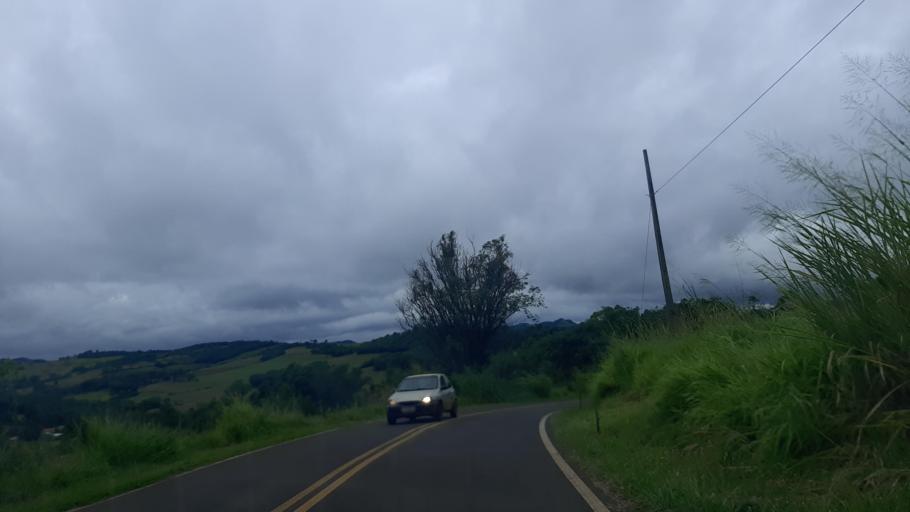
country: BR
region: Parana
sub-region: Ampere
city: Ampere
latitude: -25.9700
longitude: -53.4427
